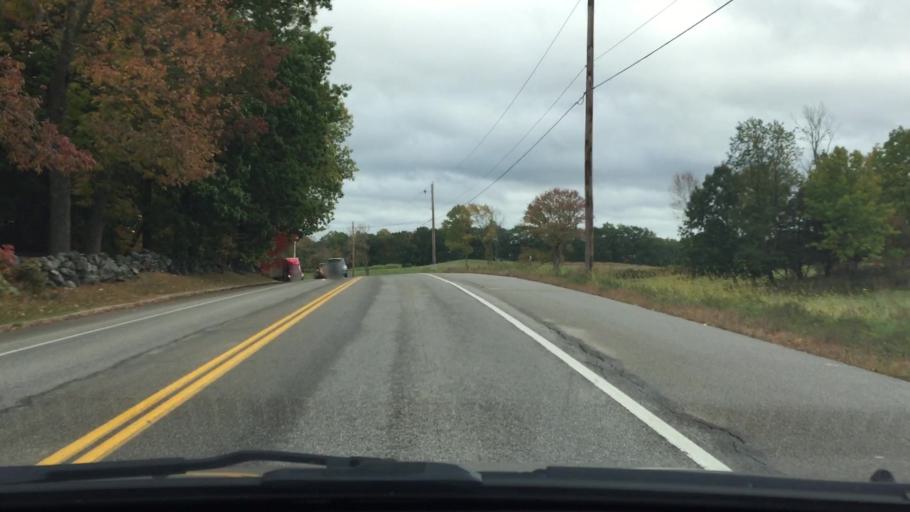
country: US
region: New Hampshire
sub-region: Strafford County
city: Durham
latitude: 43.1317
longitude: -70.8790
